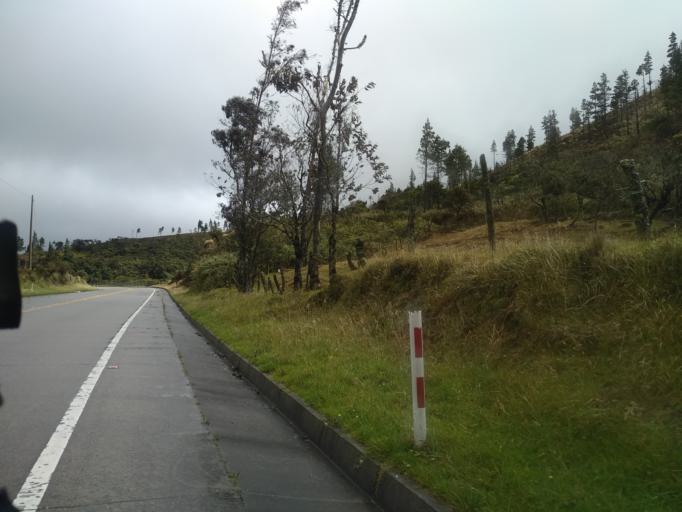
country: EC
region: Loja
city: Loja
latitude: -3.8911
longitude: -79.2622
